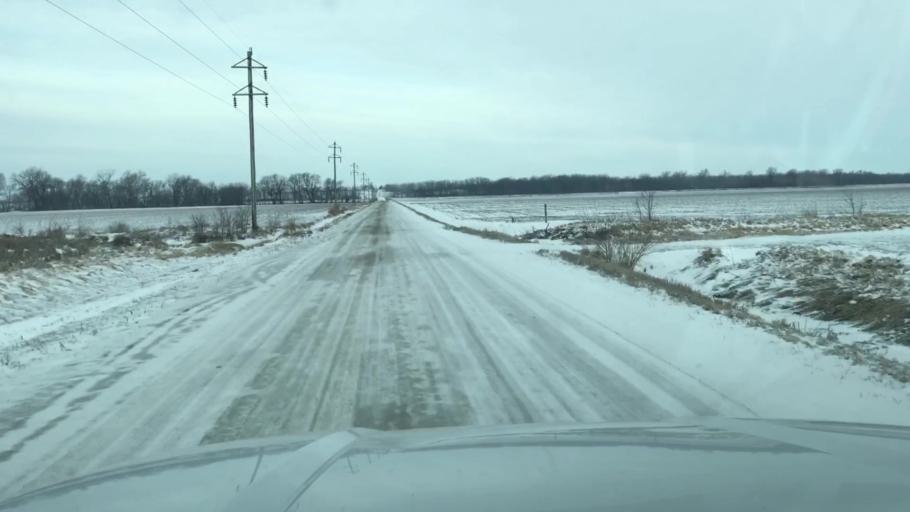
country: US
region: Missouri
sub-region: Holt County
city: Oregon
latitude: 40.1301
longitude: -95.0361
